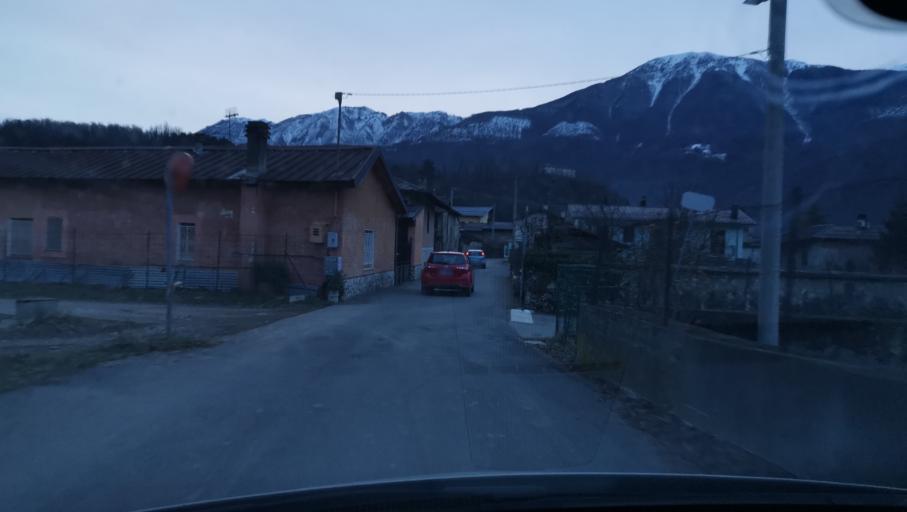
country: IT
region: Piedmont
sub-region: Provincia di Cuneo
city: Demonte
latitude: 44.3174
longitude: 7.3010
